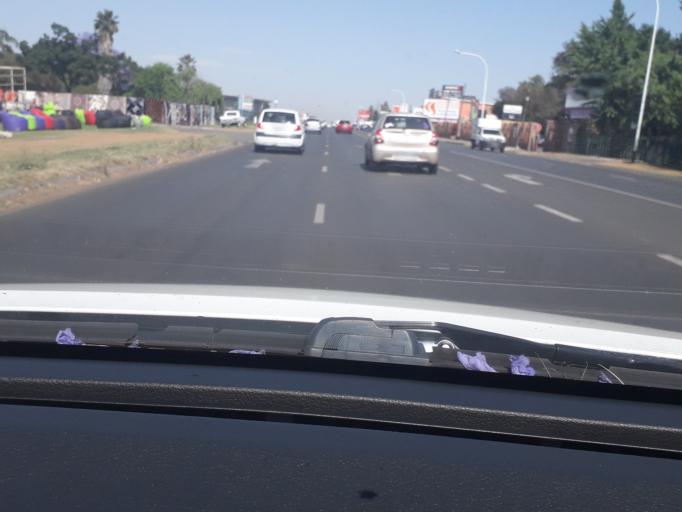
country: ZA
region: Gauteng
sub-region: Ekurhuleni Metropolitan Municipality
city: Boksburg
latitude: -26.1790
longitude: 28.2526
